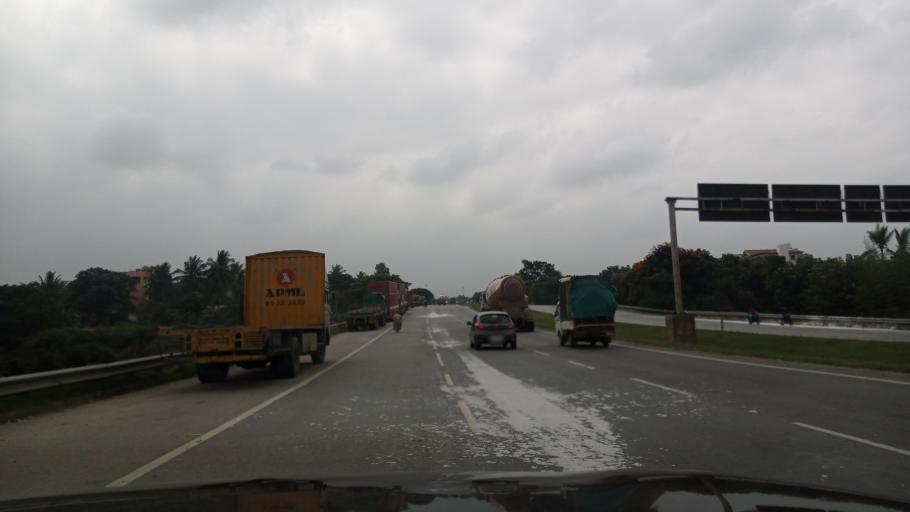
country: IN
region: Karnataka
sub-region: Bangalore Rural
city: Nelamangala
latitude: 13.0535
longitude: 77.4768
